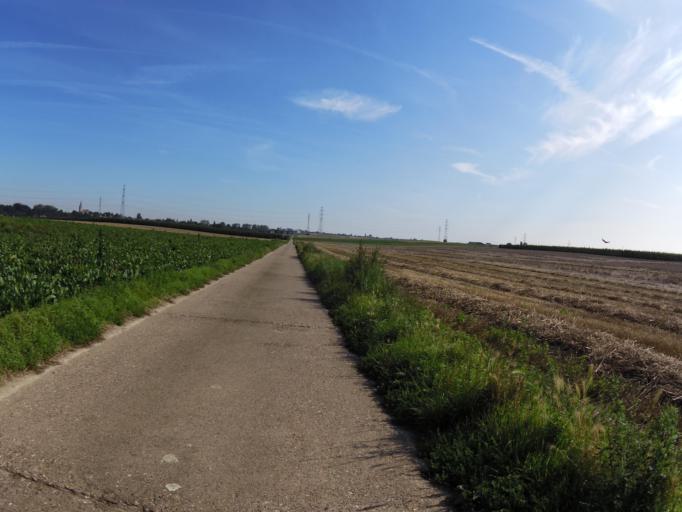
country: BE
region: Flanders
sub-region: Provincie Limburg
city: Riemst
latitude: 50.7938
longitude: 5.5638
